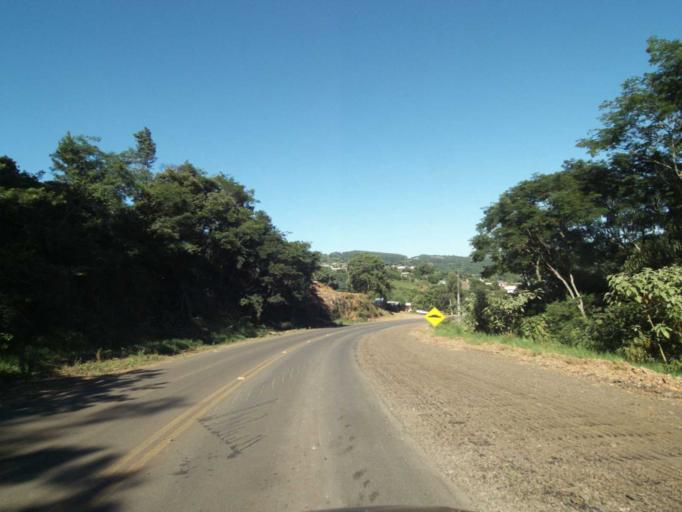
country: BR
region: Parana
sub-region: Francisco Beltrao
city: Francisco Beltrao
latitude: -26.1446
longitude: -53.3048
